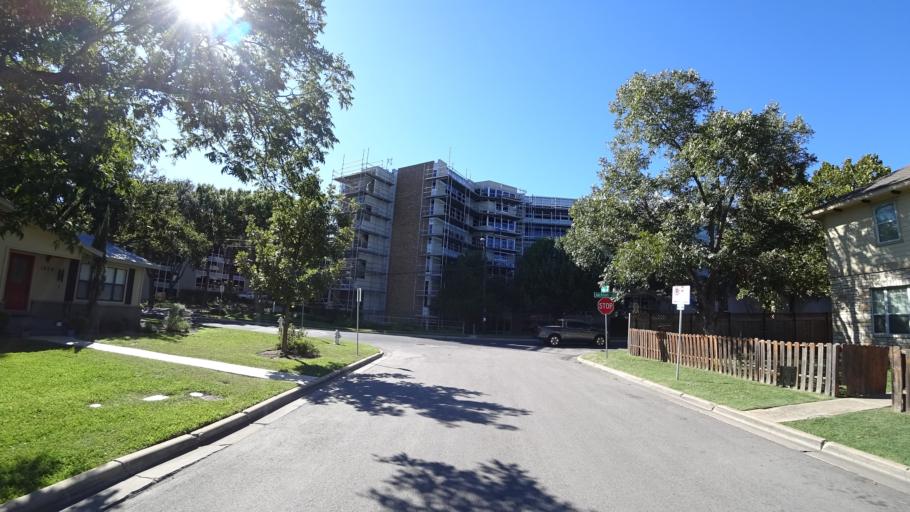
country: US
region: Texas
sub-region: Travis County
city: Austin
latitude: 30.3152
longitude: -97.7548
